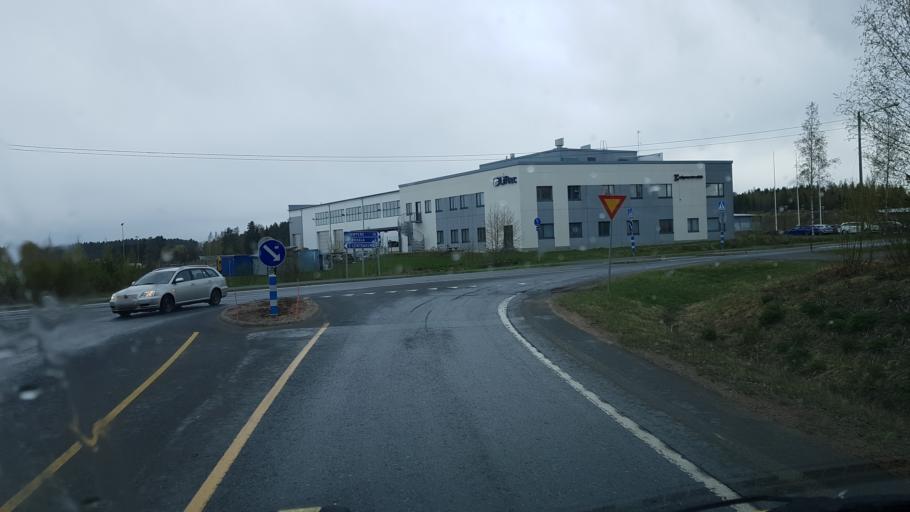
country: FI
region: Pirkanmaa
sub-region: Tampere
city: Pirkkala
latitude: 61.4301
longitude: 23.6216
